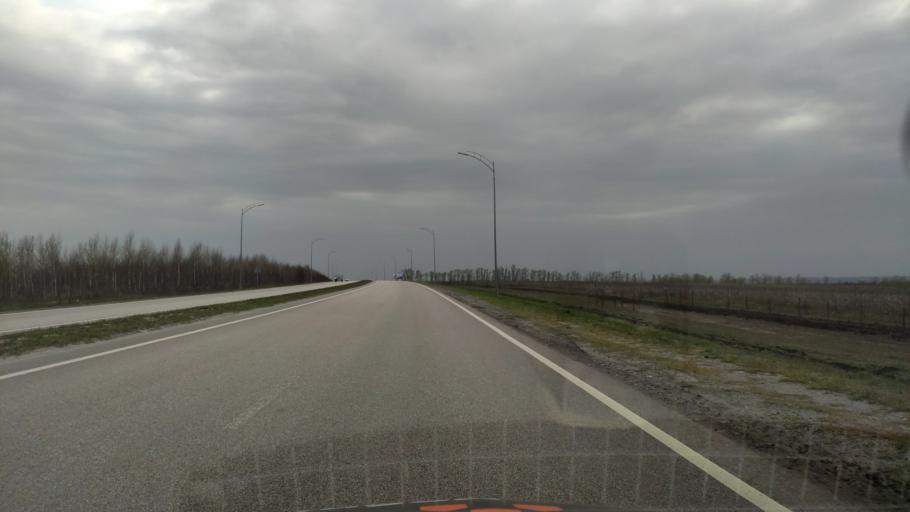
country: RU
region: Belgorod
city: Staryy Oskol
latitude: 51.3810
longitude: 37.8549
